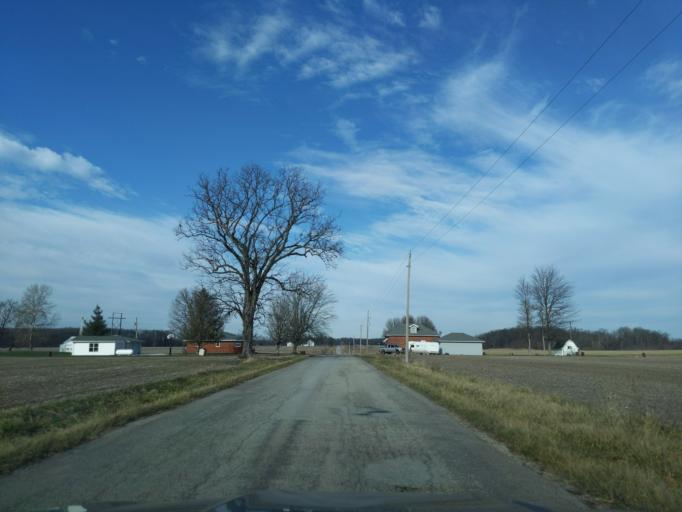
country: US
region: Indiana
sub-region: Decatur County
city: Greensburg
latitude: 39.2504
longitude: -85.4192
